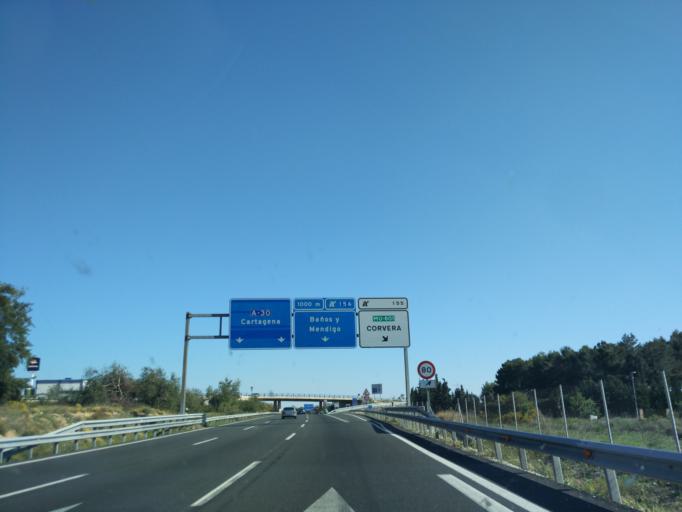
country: ES
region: Murcia
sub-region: Murcia
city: Murcia
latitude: 37.8873
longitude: -1.1401
